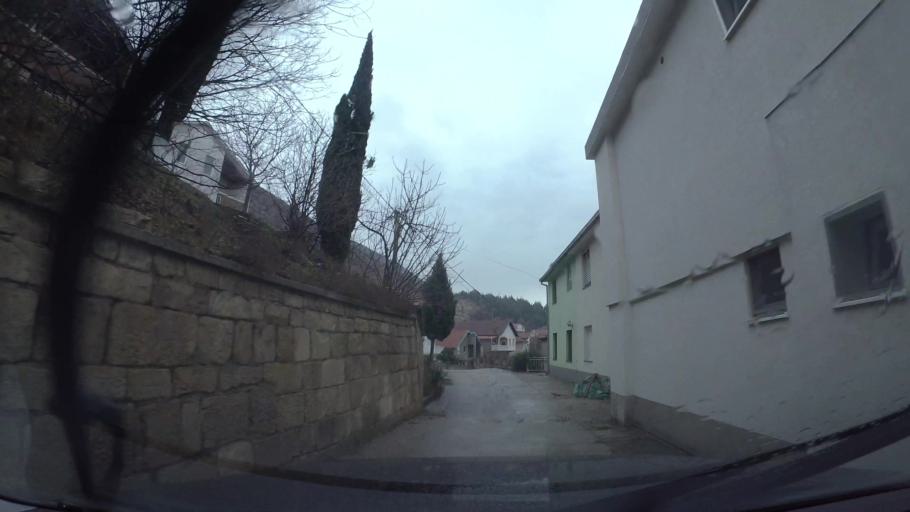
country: BA
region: Federation of Bosnia and Herzegovina
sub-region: Hercegovacko-Bosanski Kanton
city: Mostar
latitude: 43.3423
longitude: 17.8192
